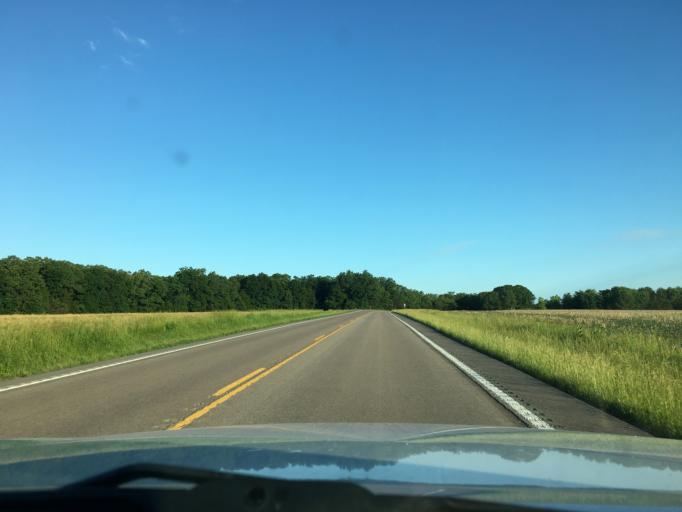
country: US
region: Missouri
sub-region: Gasconade County
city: Owensville
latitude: 38.4554
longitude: -91.4594
